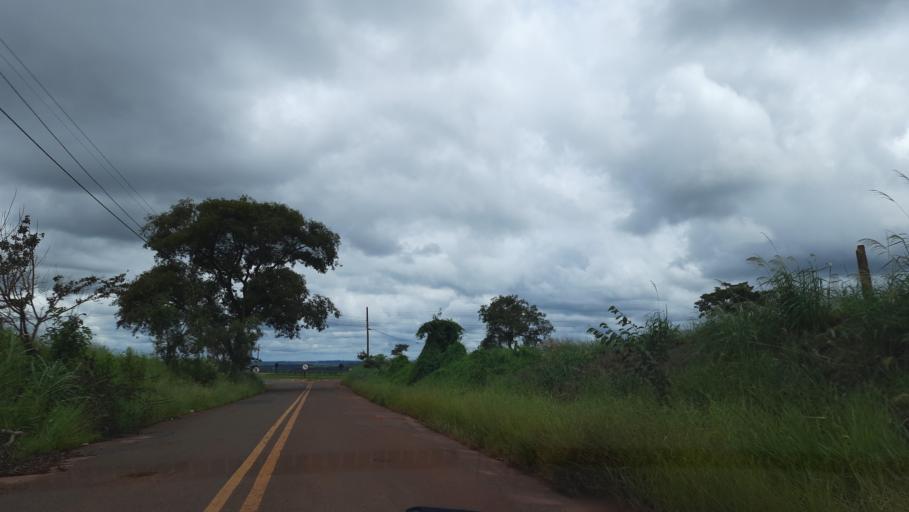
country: BR
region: Sao Paulo
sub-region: Casa Branca
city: Casa Branca
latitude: -21.7984
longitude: -47.0962
